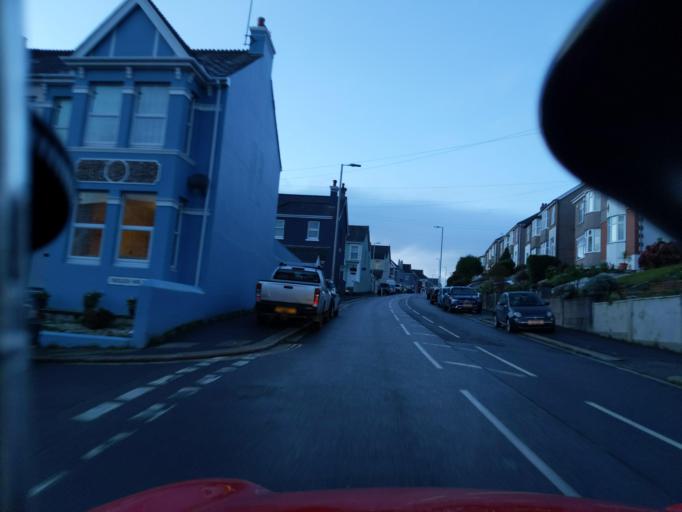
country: GB
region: England
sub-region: Plymouth
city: Plymouth
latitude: 50.3918
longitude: -4.1405
